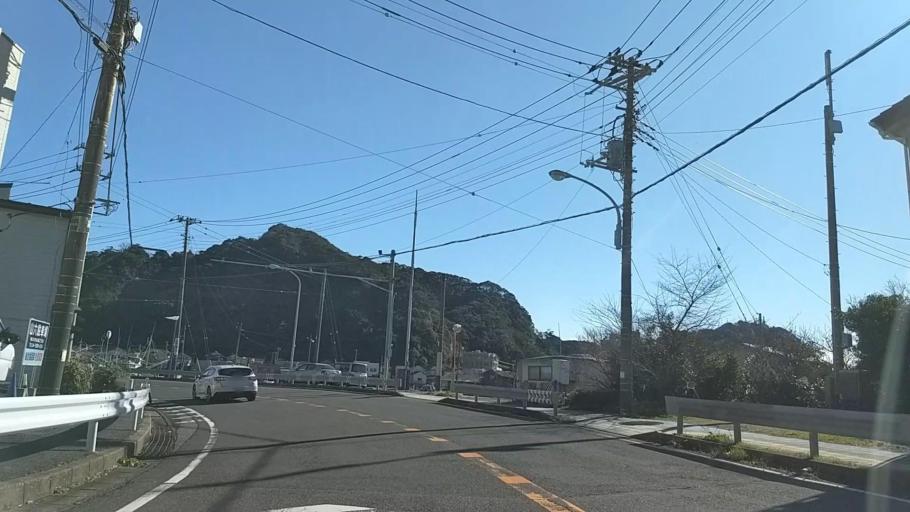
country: JP
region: Chiba
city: Kawaguchi
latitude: 35.1237
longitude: 140.1957
